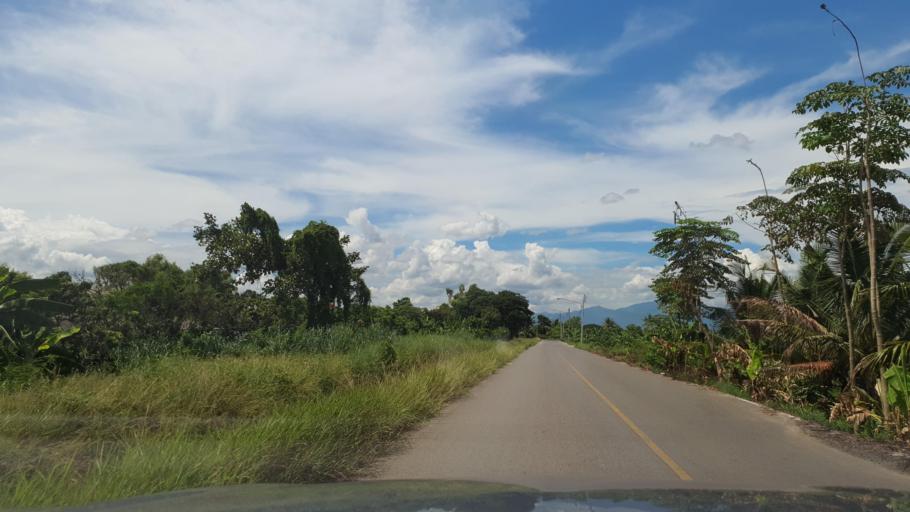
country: TH
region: Chiang Mai
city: San Pa Tong
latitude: 18.5928
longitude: 98.9052
